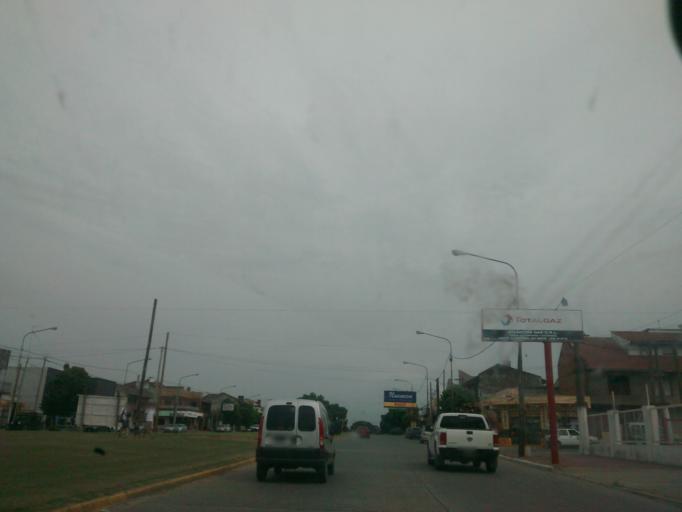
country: AR
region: Buenos Aires
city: Necochea
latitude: -38.5682
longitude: -58.7212
